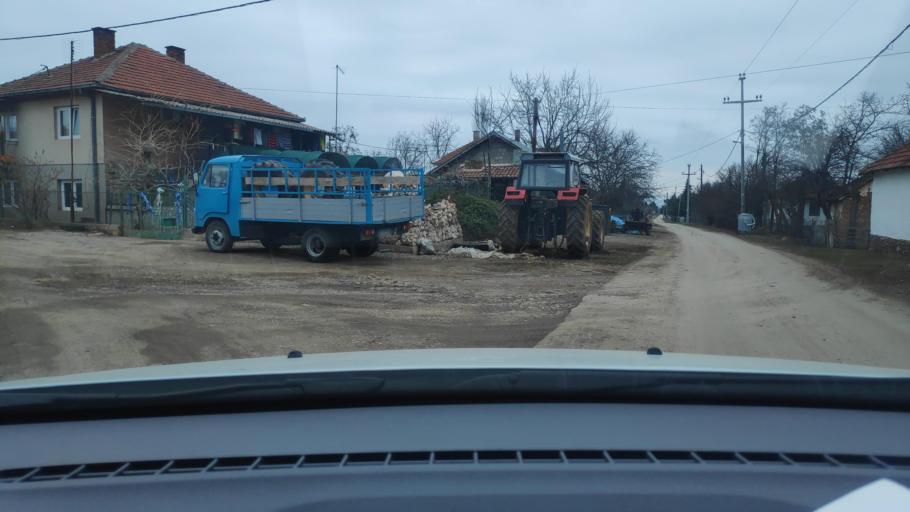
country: MK
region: Opstina Lipkovo
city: Matejche
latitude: 42.0848
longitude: 21.6219
